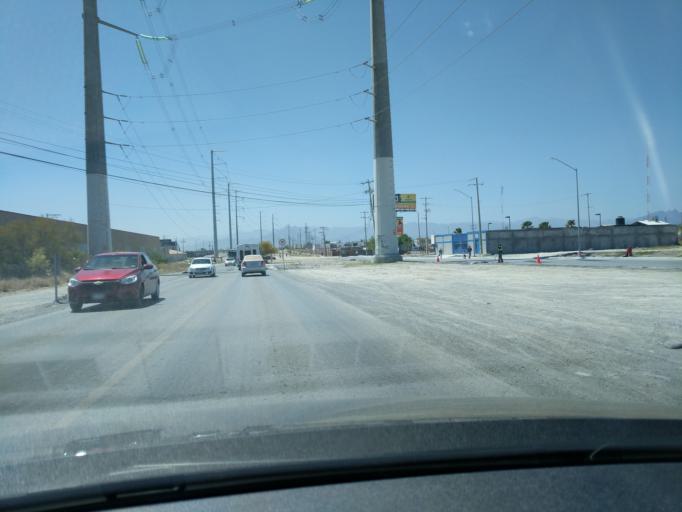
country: MX
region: Nuevo Leon
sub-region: Apodaca
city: Artemio Trevino
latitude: 25.8402
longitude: -100.1368
